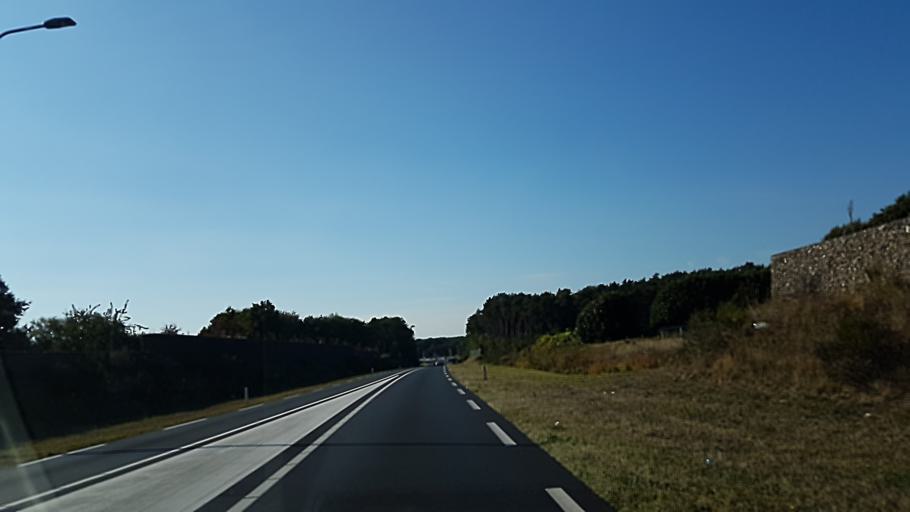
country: NL
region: North Brabant
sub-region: Gemeente Woensdrecht
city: Woensdrecht
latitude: 51.4369
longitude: 4.3277
